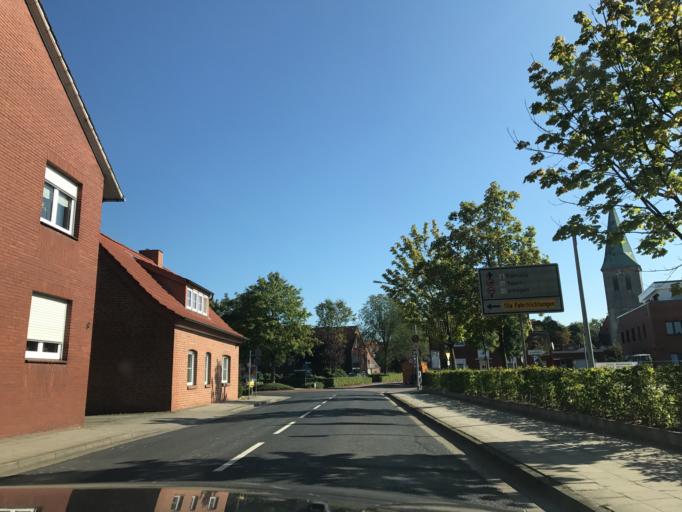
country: DE
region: Lower Saxony
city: Haselunne
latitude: 52.6720
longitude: 7.4825
